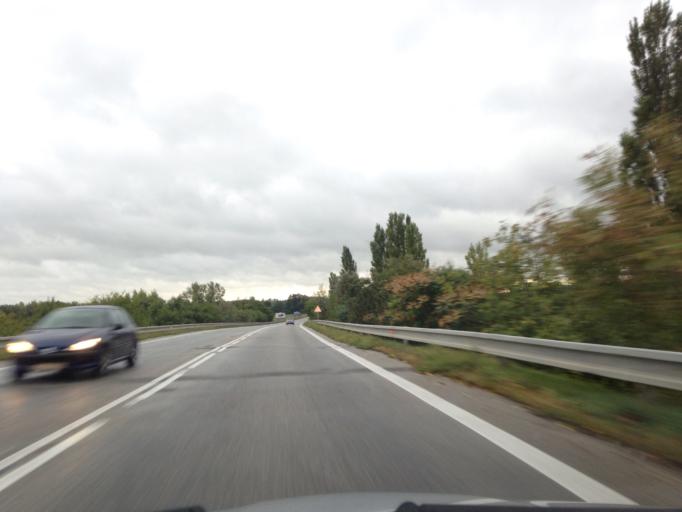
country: SK
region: Nitriansky
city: Komarno
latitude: 47.7766
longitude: 18.1601
